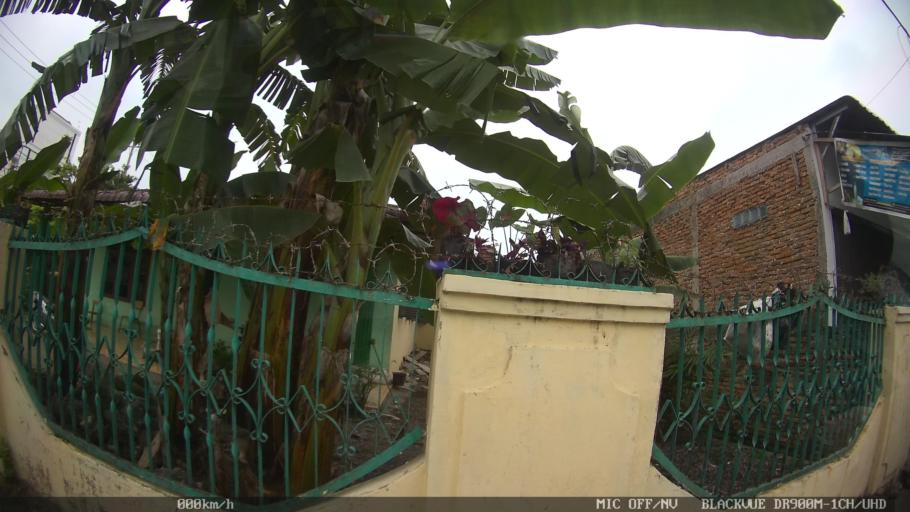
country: ID
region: North Sumatra
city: Medan
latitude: 3.5630
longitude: 98.6974
